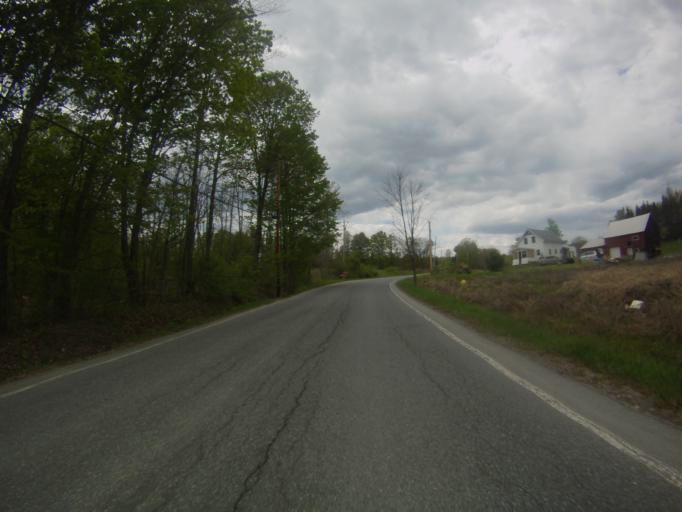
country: US
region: New York
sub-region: Essex County
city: Port Henry
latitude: 43.9508
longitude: -73.4784
